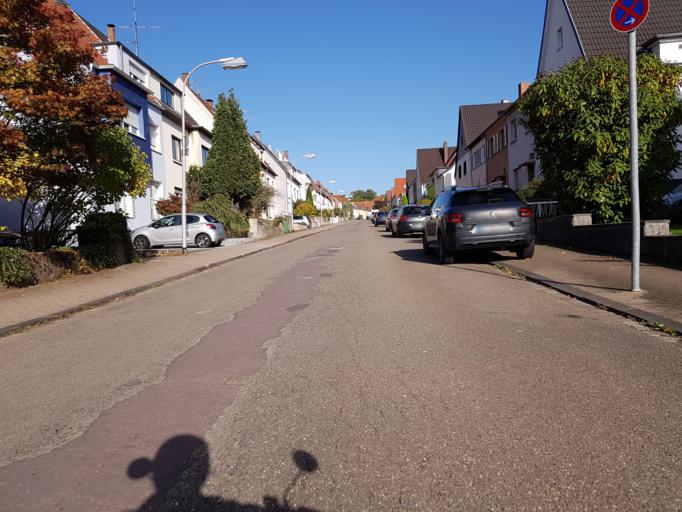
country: DE
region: Saarland
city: Saarbrucken
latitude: 49.2504
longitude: 6.9916
